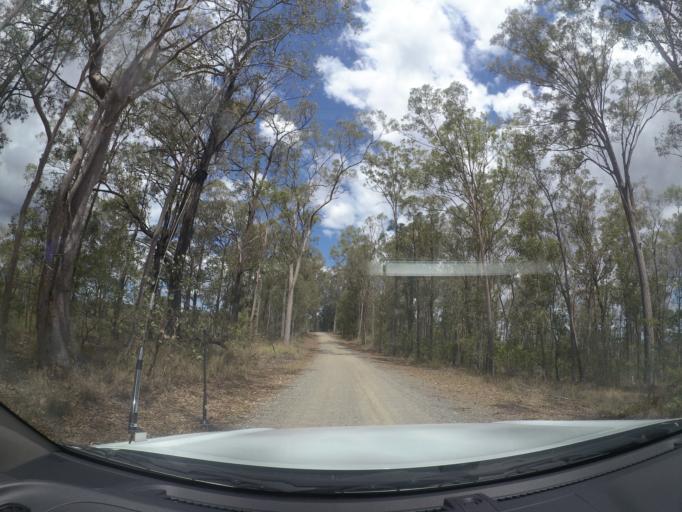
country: AU
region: Queensland
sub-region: Logan
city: Cedar Vale
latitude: -27.9081
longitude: 153.0308
